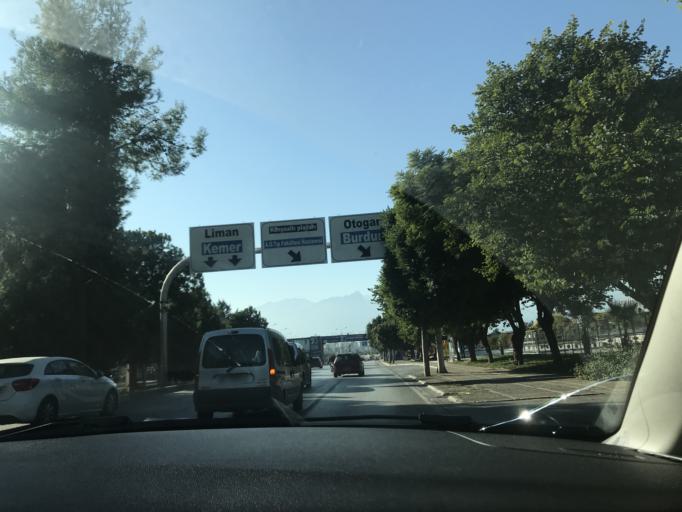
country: TR
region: Antalya
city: Antalya
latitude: 36.8865
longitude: 30.6695
